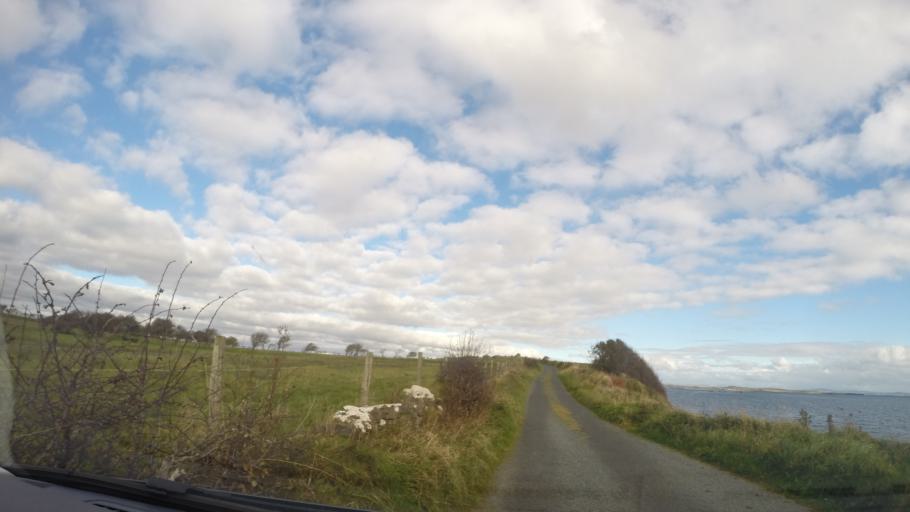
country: IE
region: Ulster
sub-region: County Donegal
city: Killybegs
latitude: 54.6052
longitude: -8.3768
